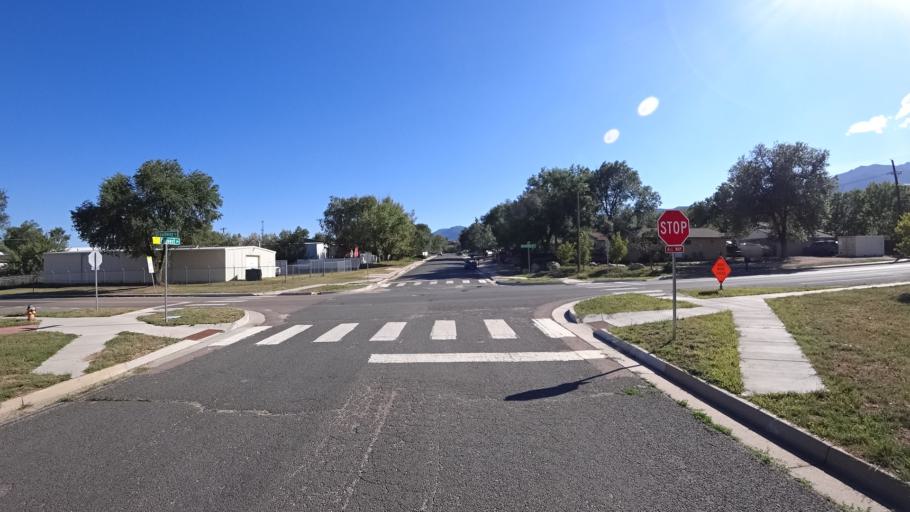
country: US
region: Colorado
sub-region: El Paso County
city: Colorado Springs
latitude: 38.8375
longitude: -104.8644
